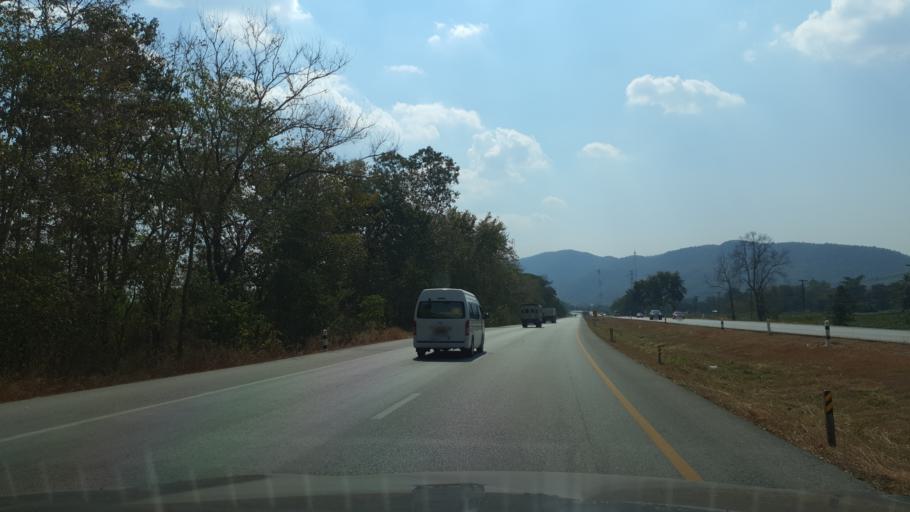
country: TH
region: Lampang
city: Mae Phrik
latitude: 17.3735
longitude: 99.1491
